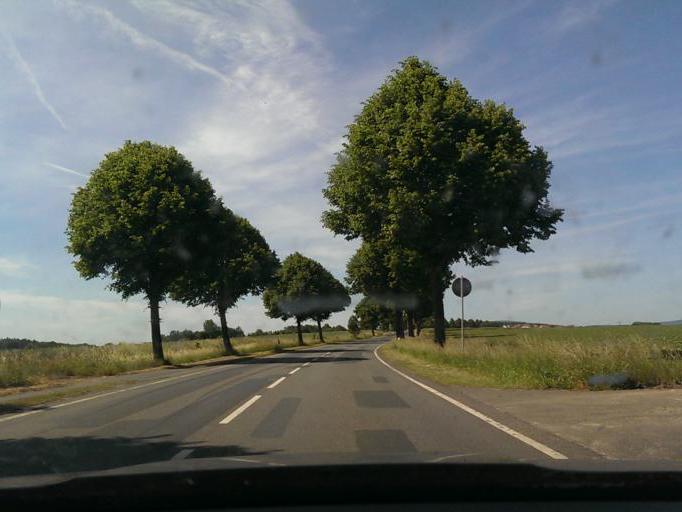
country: DE
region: Lower Saxony
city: Nordstemmen
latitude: 52.1428
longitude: 9.7604
